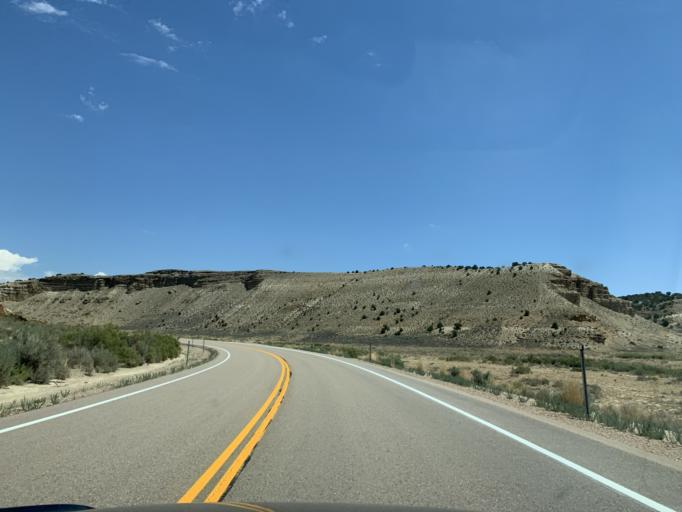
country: US
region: Utah
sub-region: Duchesne County
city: Duchesne
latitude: 39.9734
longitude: -110.1643
